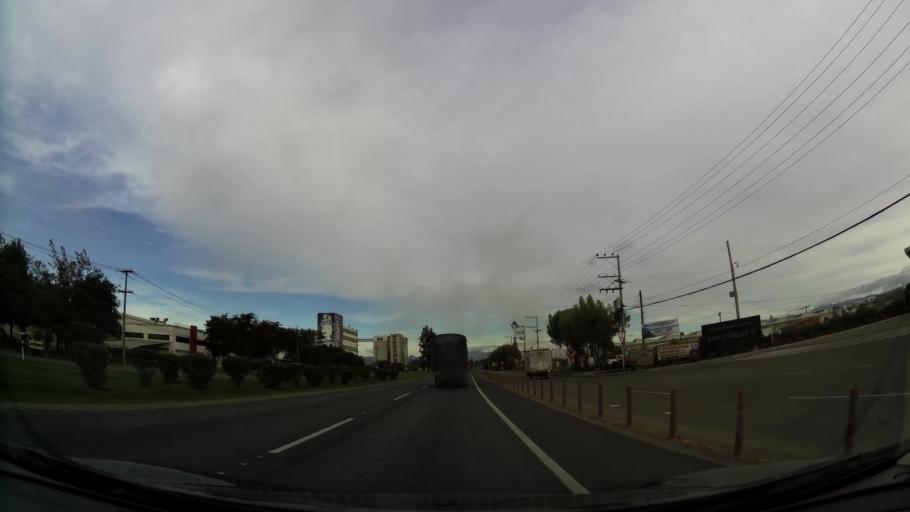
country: CO
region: Cundinamarca
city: Mosquera
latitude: 4.7002
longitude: -74.2231
